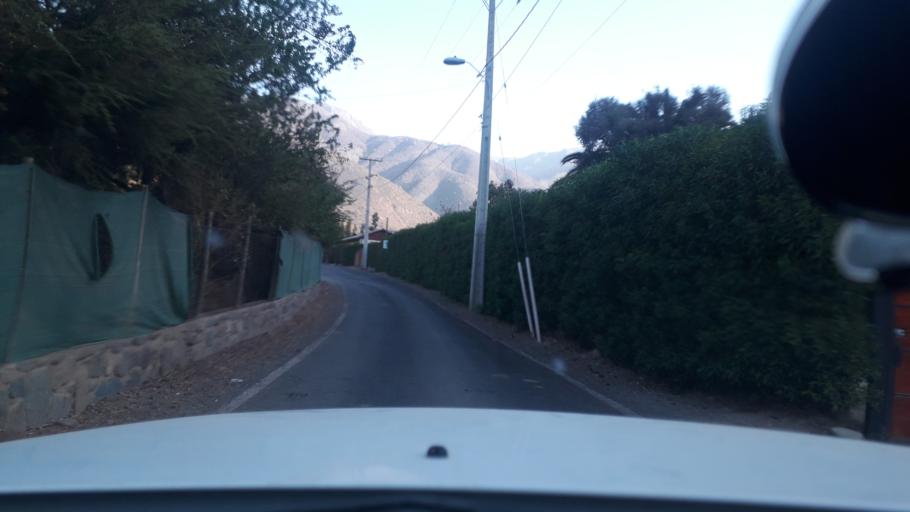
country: CL
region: Valparaiso
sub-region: Provincia de Marga Marga
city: Limache
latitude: -33.0625
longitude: -71.1173
